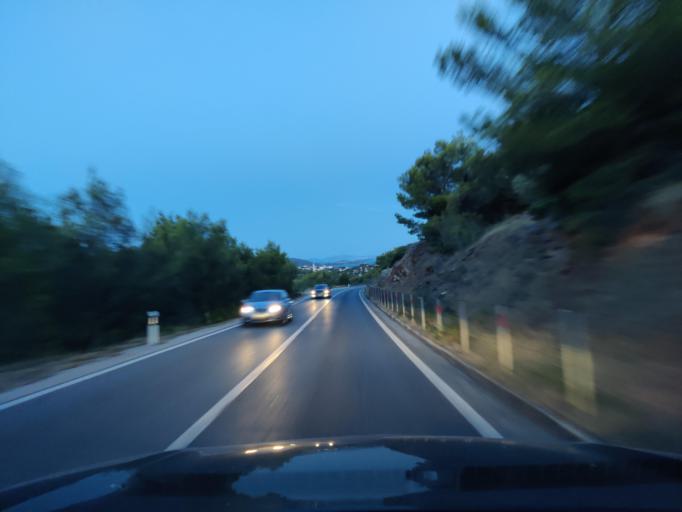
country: HR
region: Sibensko-Kniniska
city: Murter
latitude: 43.7962
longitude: 15.6205
